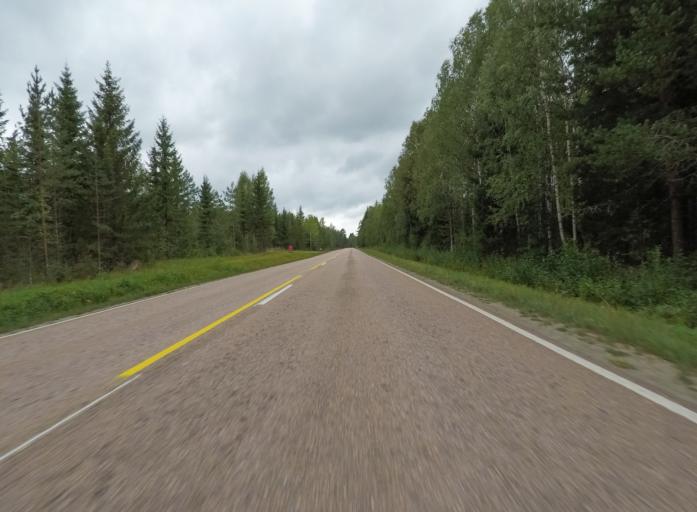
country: FI
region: Central Finland
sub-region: Jyvaeskylae
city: Hankasalmi
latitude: 62.3593
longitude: 26.5523
